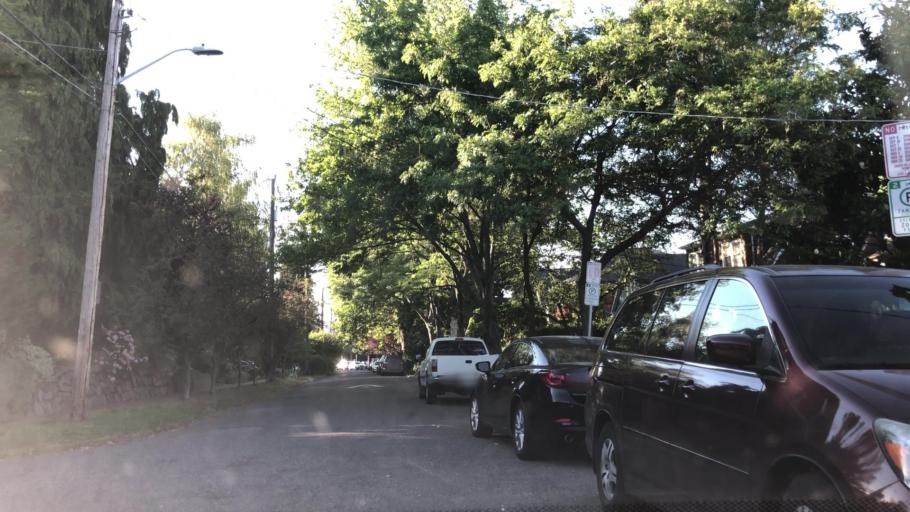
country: US
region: Washington
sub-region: King County
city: Seattle
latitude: 47.6378
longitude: -122.3028
